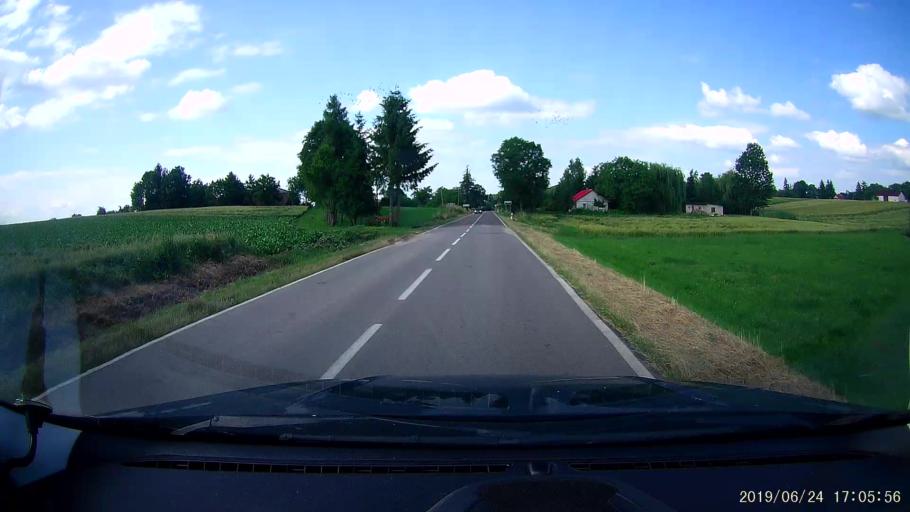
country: PL
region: Lublin Voivodeship
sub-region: Powiat hrubieszowski
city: Dolhobyczow
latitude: 50.5820
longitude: 23.9685
